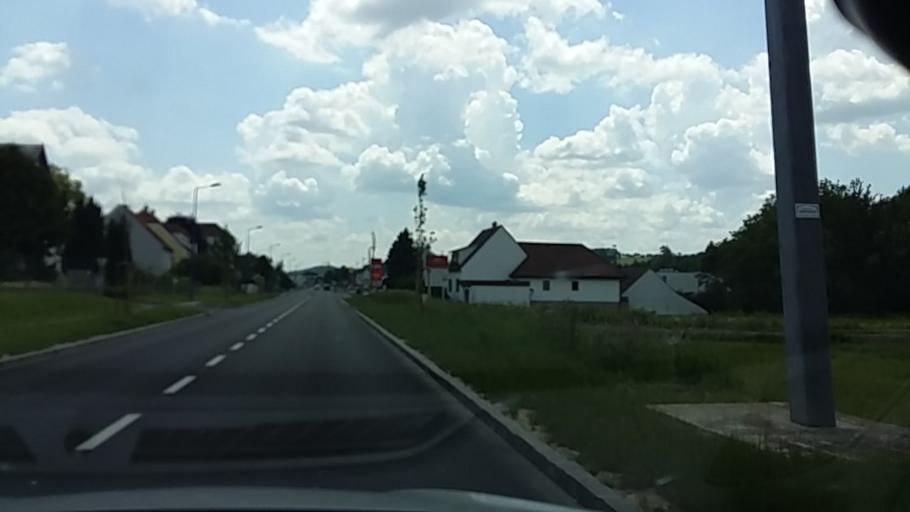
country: AT
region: Burgenland
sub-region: Politischer Bezirk Gussing
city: Stegersbach
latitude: 47.1657
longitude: 16.1636
